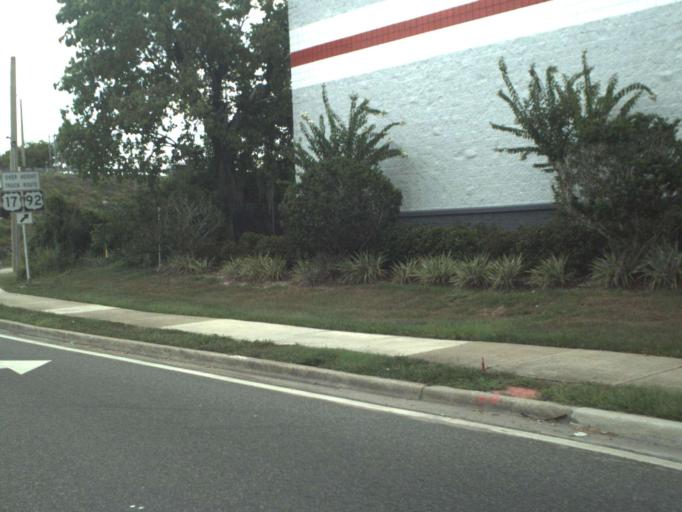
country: US
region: Florida
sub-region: Orange County
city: Eatonville
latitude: 28.6059
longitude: -81.3855
